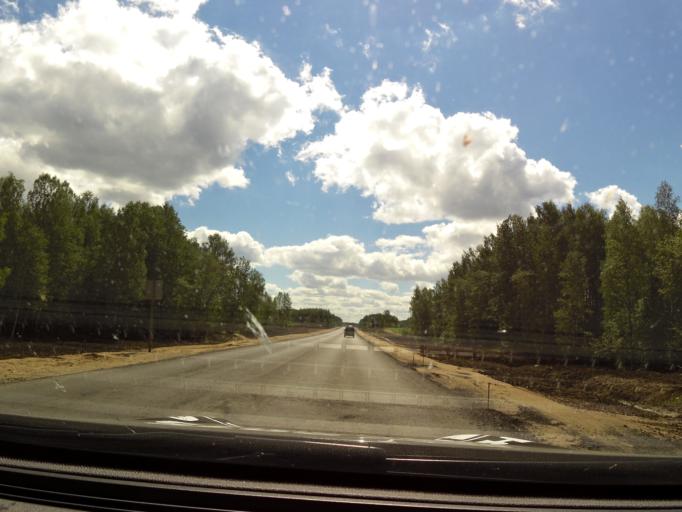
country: RU
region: Vologda
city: Molochnoye
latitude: 59.3598
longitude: 39.6743
